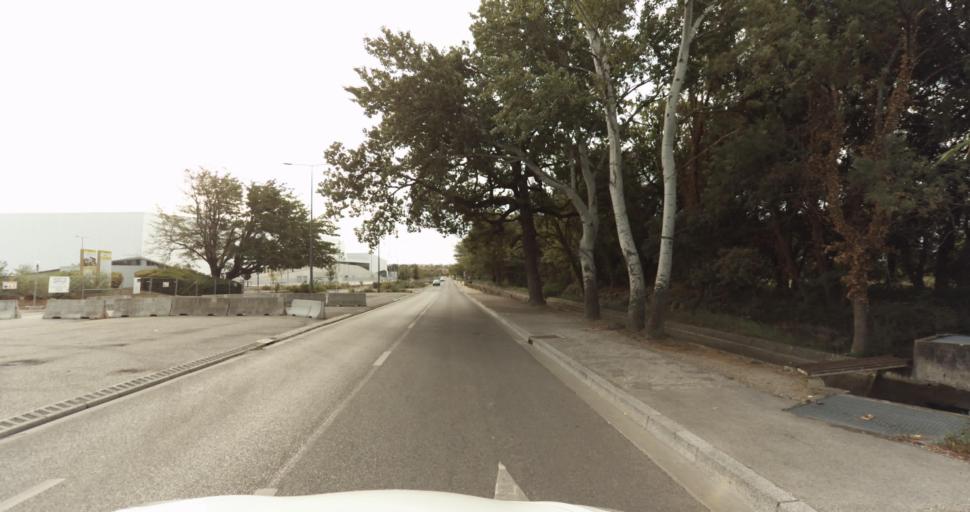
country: FR
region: Provence-Alpes-Cote d'Azur
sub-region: Departement des Bouches-du-Rhone
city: Miramas
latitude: 43.5944
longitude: 4.9968
